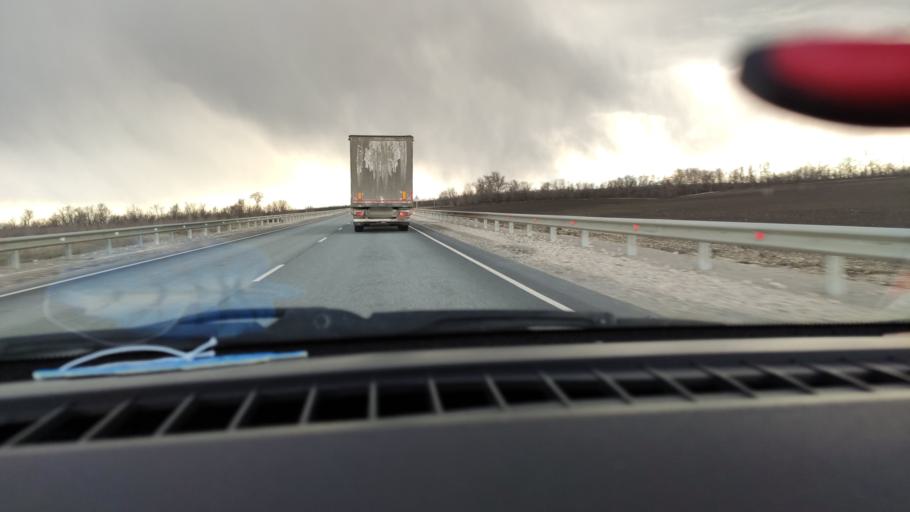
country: RU
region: Saratov
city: Yelshanka
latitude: 51.8462
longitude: 46.4837
